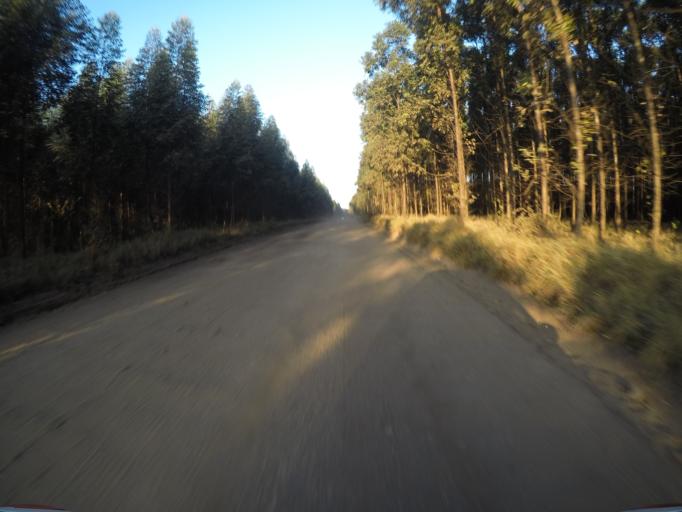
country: ZA
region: KwaZulu-Natal
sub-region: uThungulu District Municipality
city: KwaMbonambi
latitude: -28.6694
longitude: 32.0792
